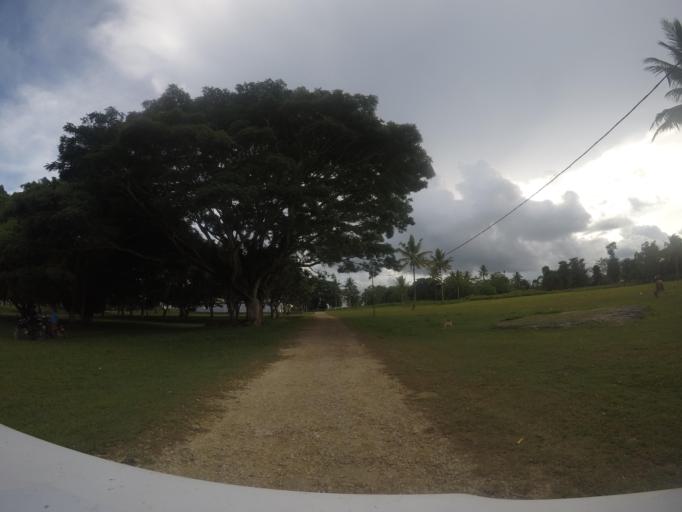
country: TL
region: Lautem
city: Lospalos
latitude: -8.5070
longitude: 126.9864
